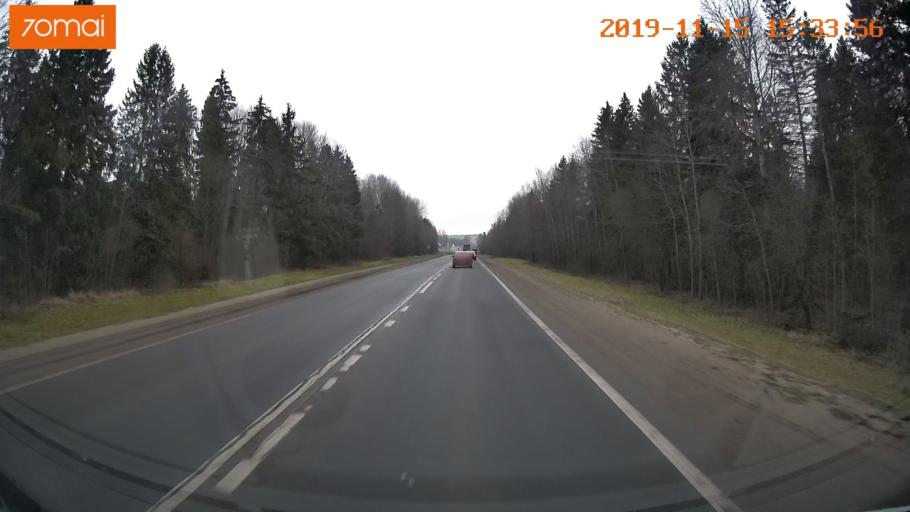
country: RU
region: Jaroslavl
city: Danilov
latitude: 58.0750
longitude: 40.0908
